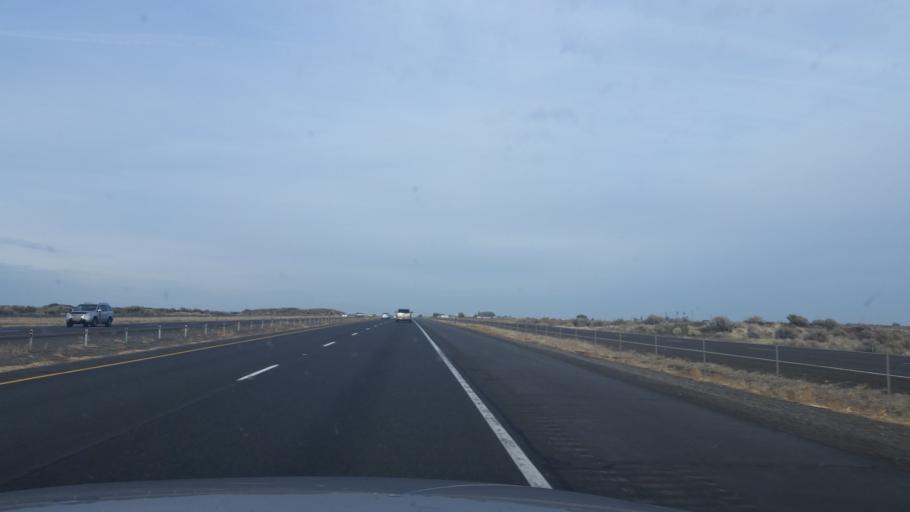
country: US
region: Washington
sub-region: Grant County
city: Quincy
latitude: 47.0366
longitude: -119.9255
